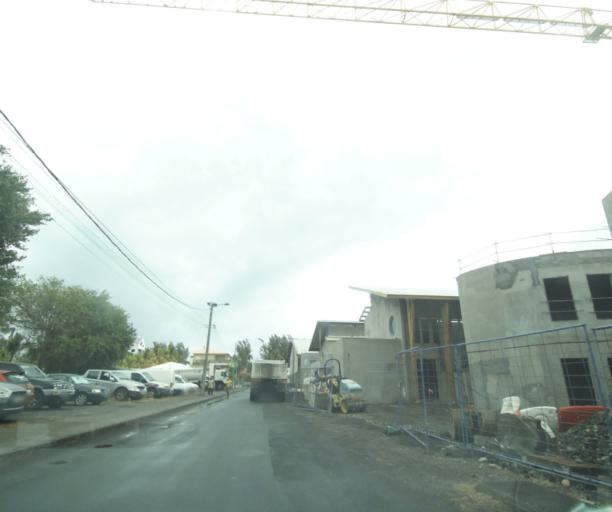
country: RE
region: Reunion
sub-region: Reunion
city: Saint-Paul
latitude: -21.0038
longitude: 55.2782
